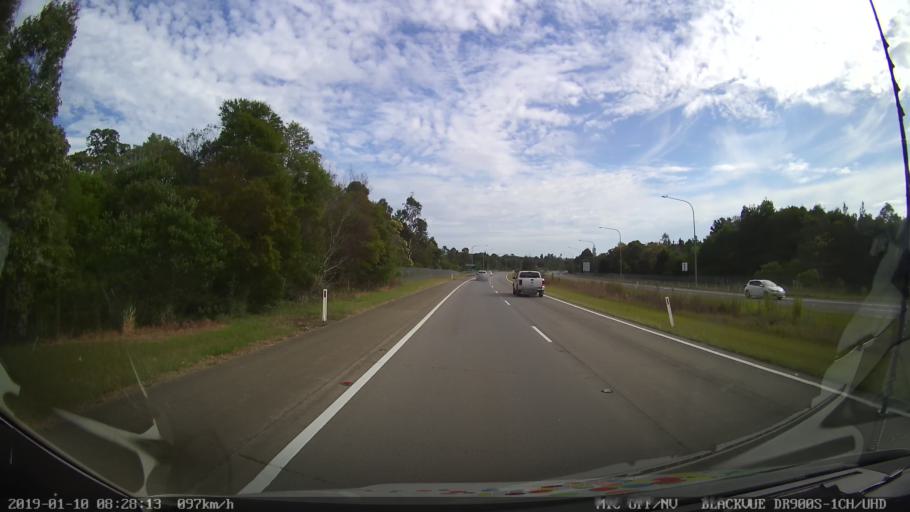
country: AU
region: New South Wales
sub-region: Coffs Harbour
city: Bonville
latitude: -30.3962
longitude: 153.0319
